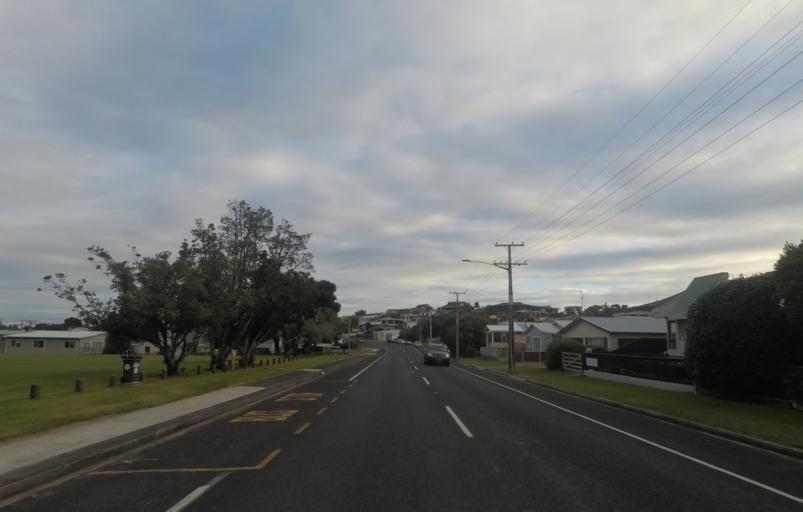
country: NZ
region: Bay of Plenty
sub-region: Western Bay of Plenty District
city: Waihi Beach
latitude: -37.4003
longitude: 175.9367
